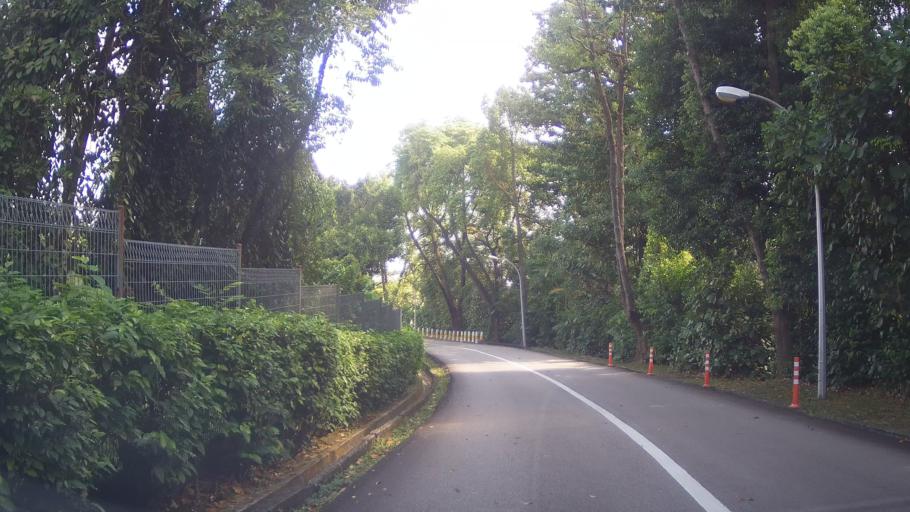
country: SG
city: Singapore
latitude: 1.3184
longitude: 103.7089
